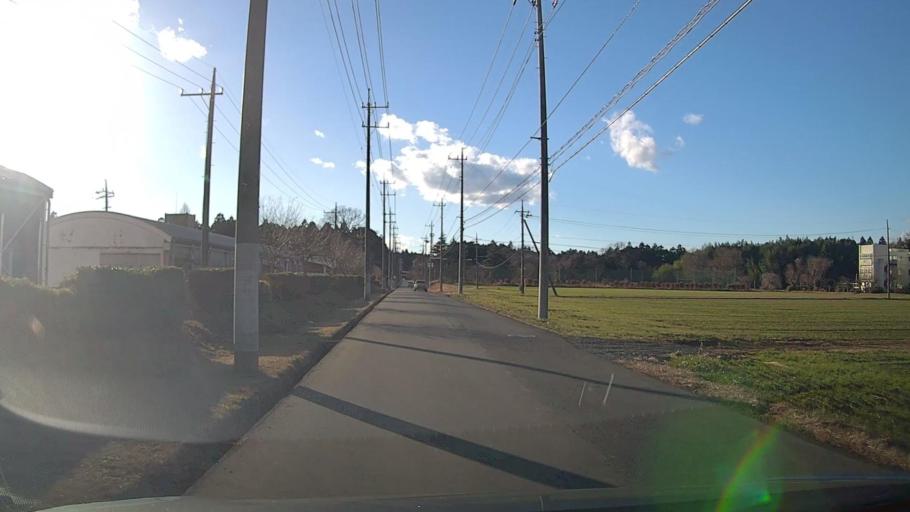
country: JP
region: Ibaraki
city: Hitachi-Naka
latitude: 36.4411
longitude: 140.4477
